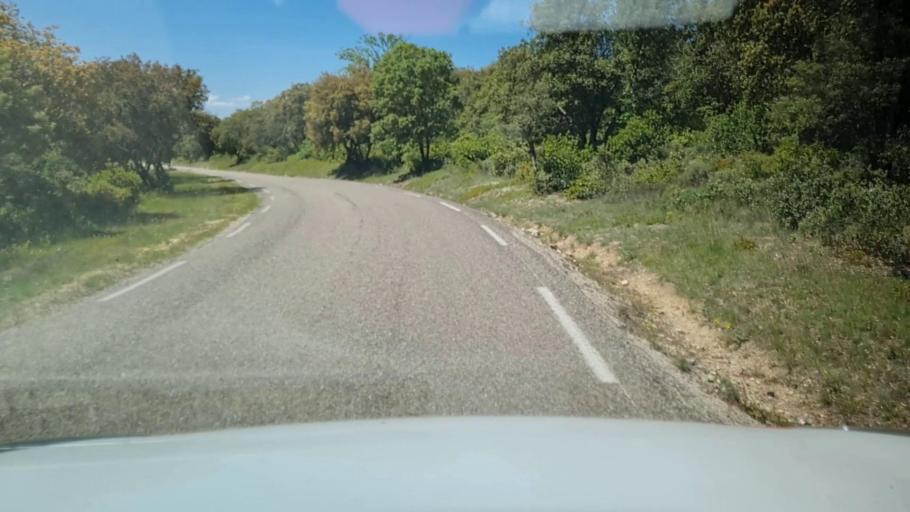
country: FR
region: Languedoc-Roussillon
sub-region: Departement du Gard
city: Clarensac
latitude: 43.8456
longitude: 4.2264
